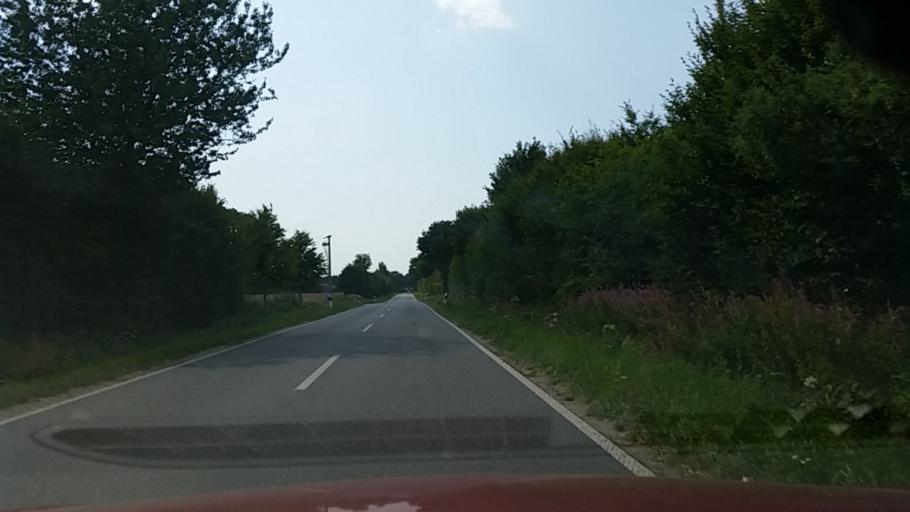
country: DE
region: Schleswig-Holstein
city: Alt Molln
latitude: 53.6180
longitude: 10.6363
